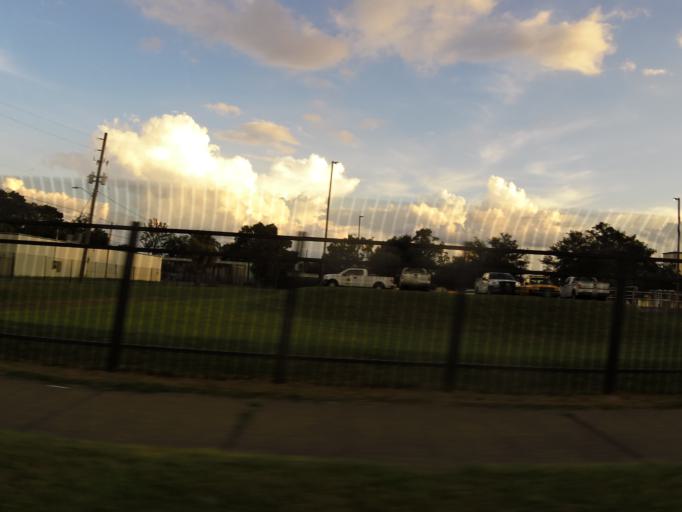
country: US
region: Florida
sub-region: Duval County
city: Jacksonville
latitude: 30.3228
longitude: -81.6873
